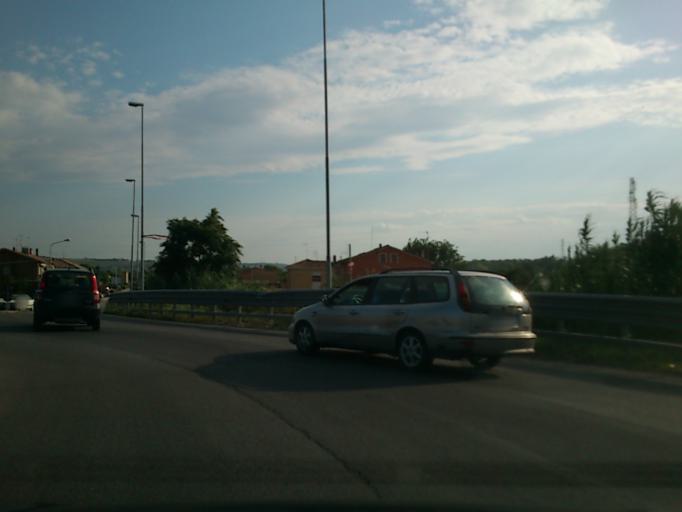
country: IT
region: The Marches
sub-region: Provincia di Pesaro e Urbino
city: Fano
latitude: 43.8261
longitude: 13.0544
